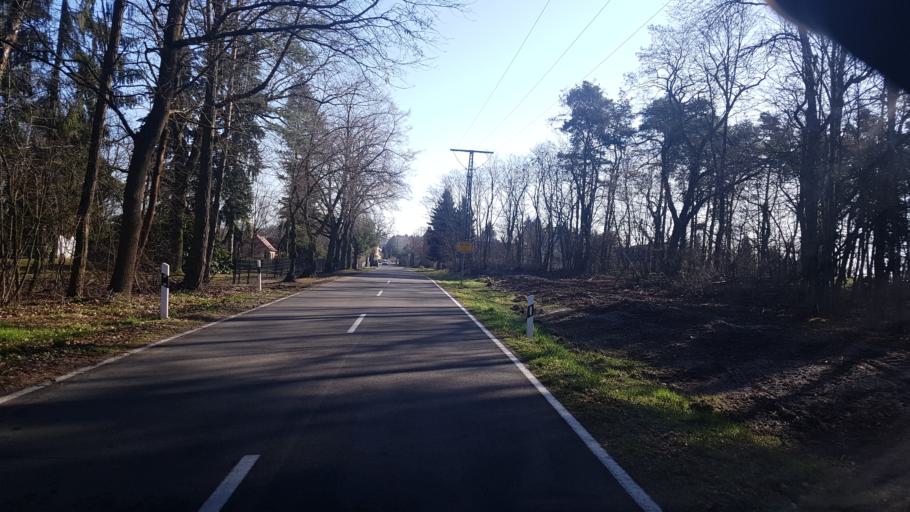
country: DE
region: Brandenburg
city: Crinitz
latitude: 51.7624
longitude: 13.7447
